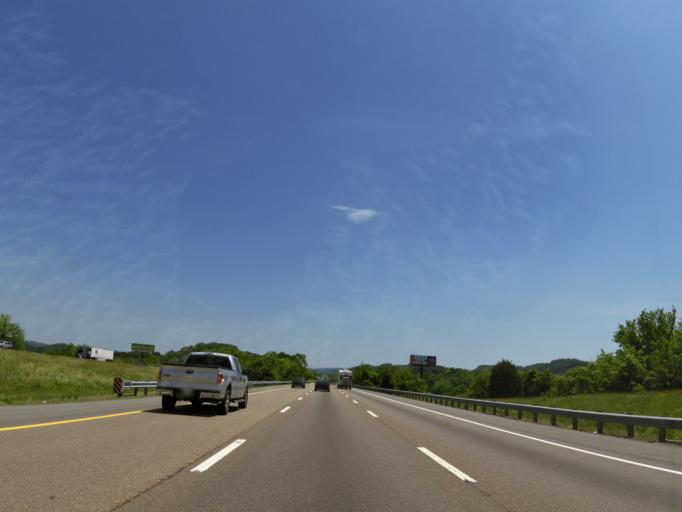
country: US
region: Tennessee
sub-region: Jefferson County
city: New Market
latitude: 35.9906
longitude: -83.5731
